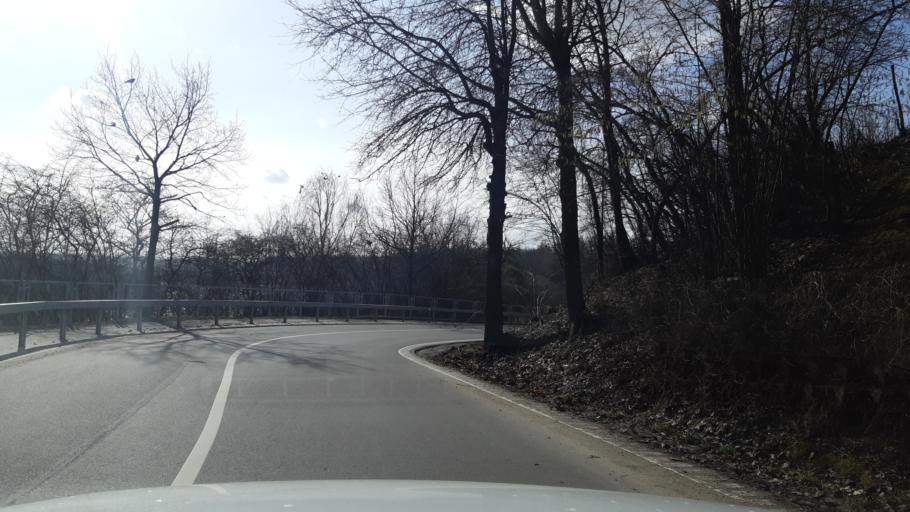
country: LT
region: Kauno apskritis
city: Dainava (Kaunas)
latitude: 54.8934
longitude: 23.9593
